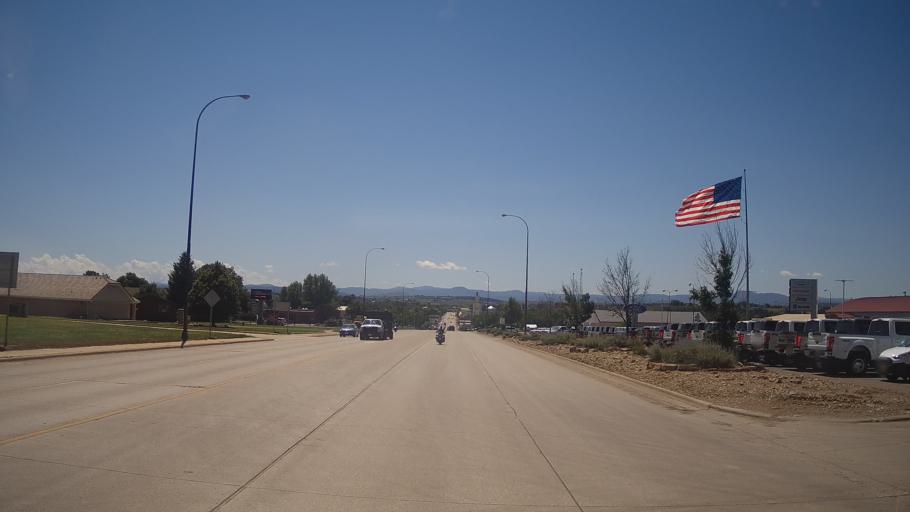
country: US
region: South Dakota
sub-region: Butte County
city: Belle Fourche
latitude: 44.6801
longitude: -103.8537
